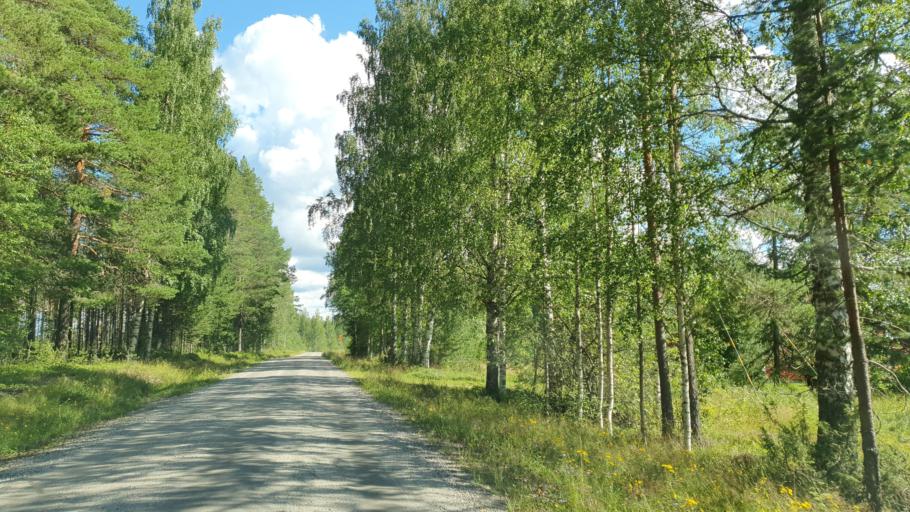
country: FI
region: Kainuu
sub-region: Kehys-Kainuu
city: Kuhmo
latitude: 64.1102
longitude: 29.3791
